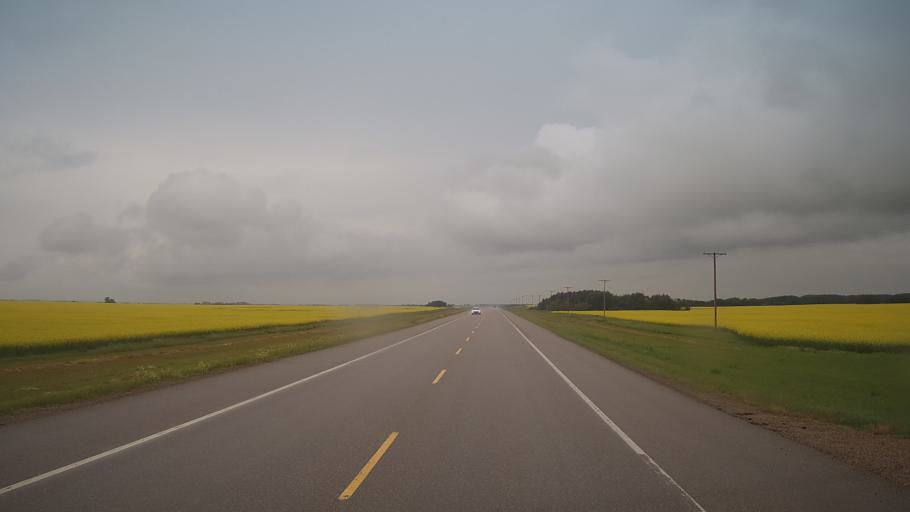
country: CA
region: Saskatchewan
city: Wilkie
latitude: 52.4249
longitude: -108.9059
